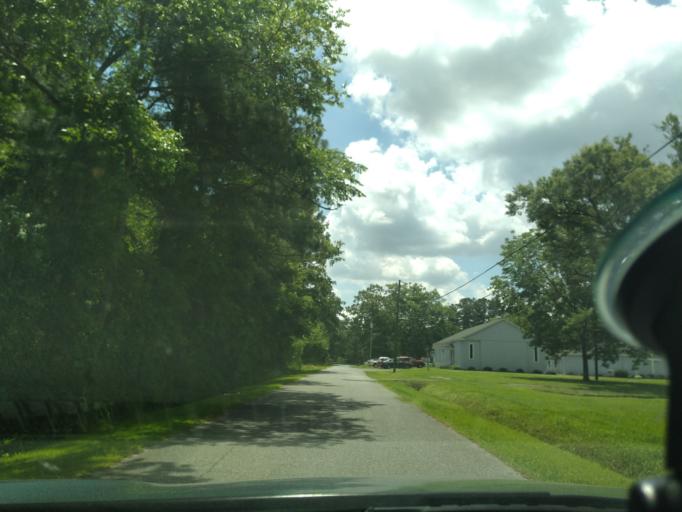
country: US
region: North Carolina
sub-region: Washington County
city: Plymouth
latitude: 35.8510
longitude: -76.7614
